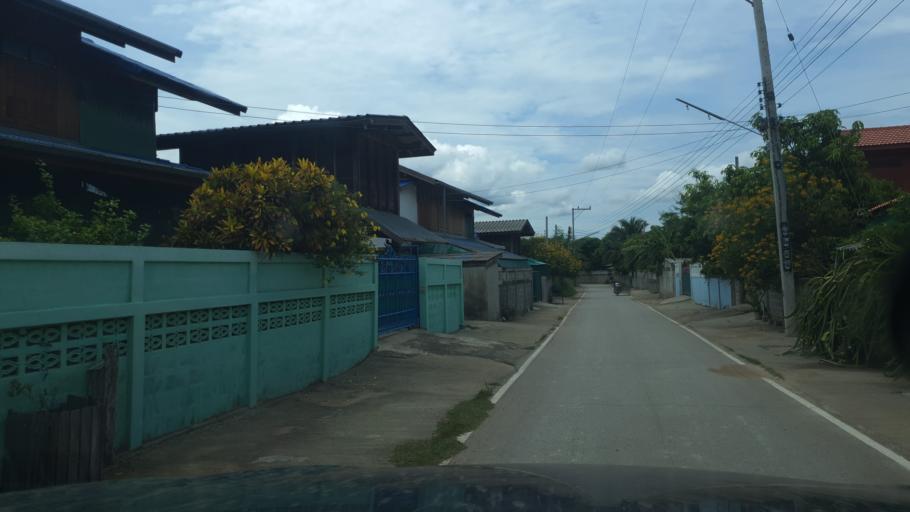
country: TH
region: Lampang
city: Sop Prap
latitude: 17.8778
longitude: 99.3836
